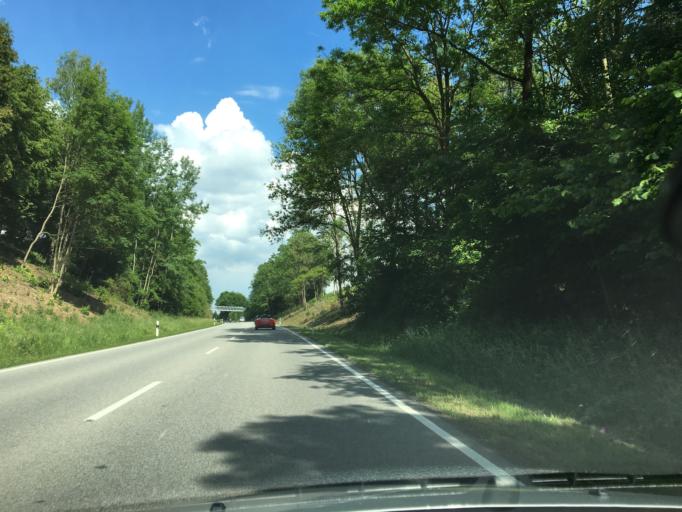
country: DE
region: Bavaria
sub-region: Upper Bavaria
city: Langenbach
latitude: 48.4339
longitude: 11.8565
